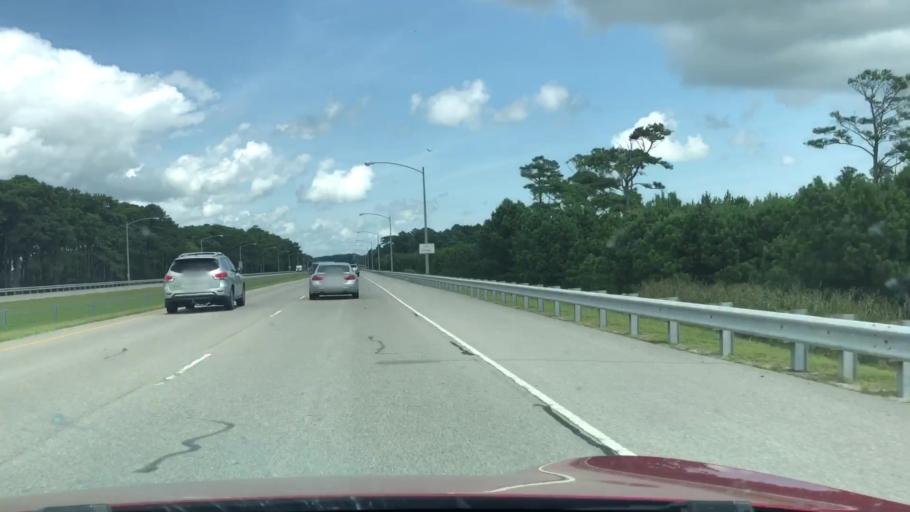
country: US
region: Virginia
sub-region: Northampton County
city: Cape Charles
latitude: 37.1218
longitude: -75.9681
